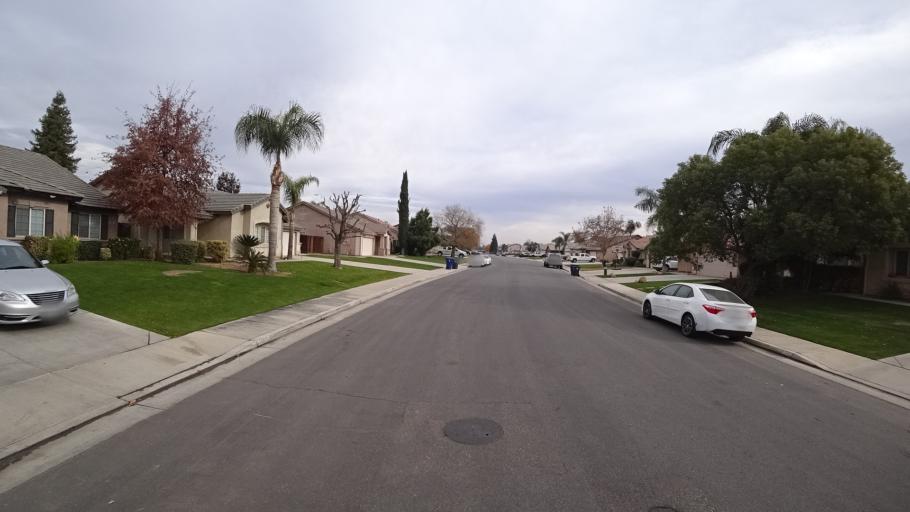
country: US
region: California
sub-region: Kern County
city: Rosedale
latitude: 35.4212
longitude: -119.1331
